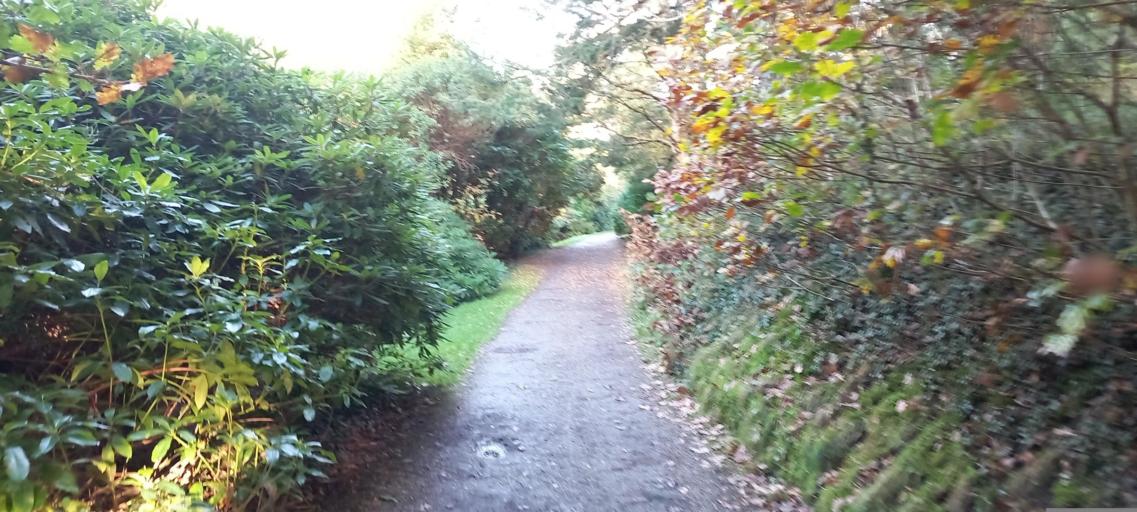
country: GB
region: Wales
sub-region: Gwynedd
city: Bangor
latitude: 53.2268
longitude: -4.0982
